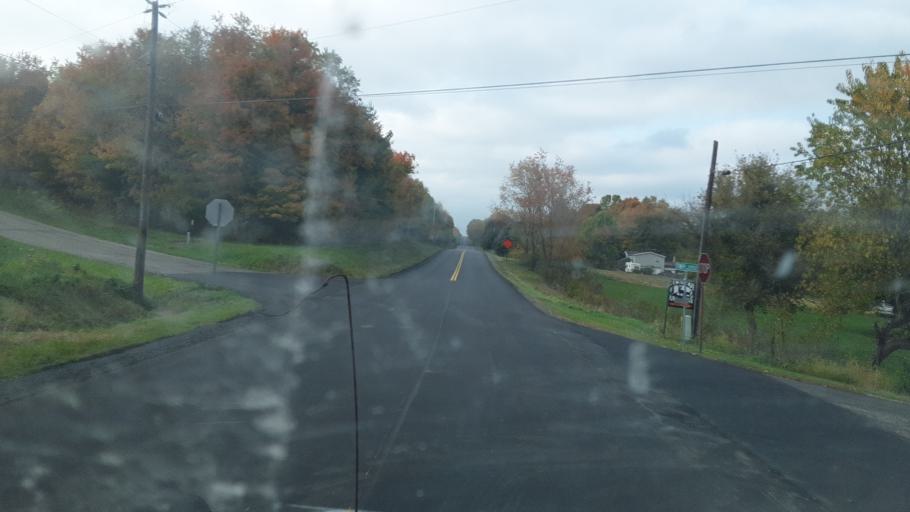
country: US
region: Ohio
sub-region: Ashland County
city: Loudonville
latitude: 40.7332
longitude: -82.1946
